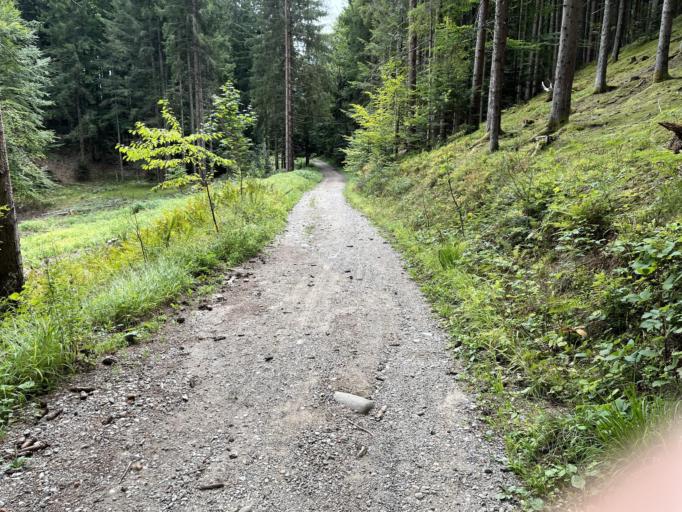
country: AT
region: Carinthia
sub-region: Politischer Bezirk Spittal an der Drau
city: Millstatt
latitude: 46.7853
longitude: 13.5565
